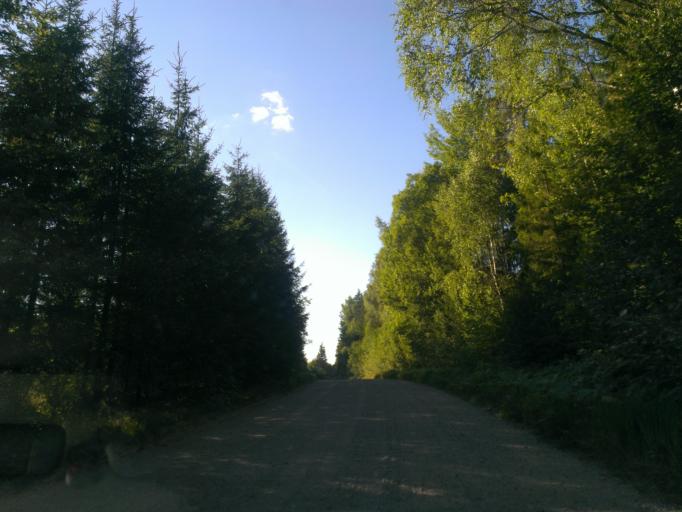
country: LV
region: Malpils
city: Malpils
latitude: 57.0966
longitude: 25.0466
